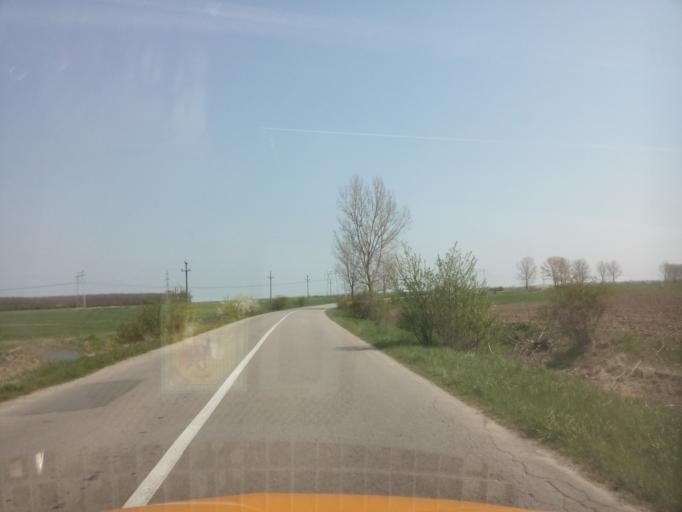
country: RO
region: Calarasi
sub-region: Comuna Soldanu
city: Soldanu
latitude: 44.2244
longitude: 26.5493
